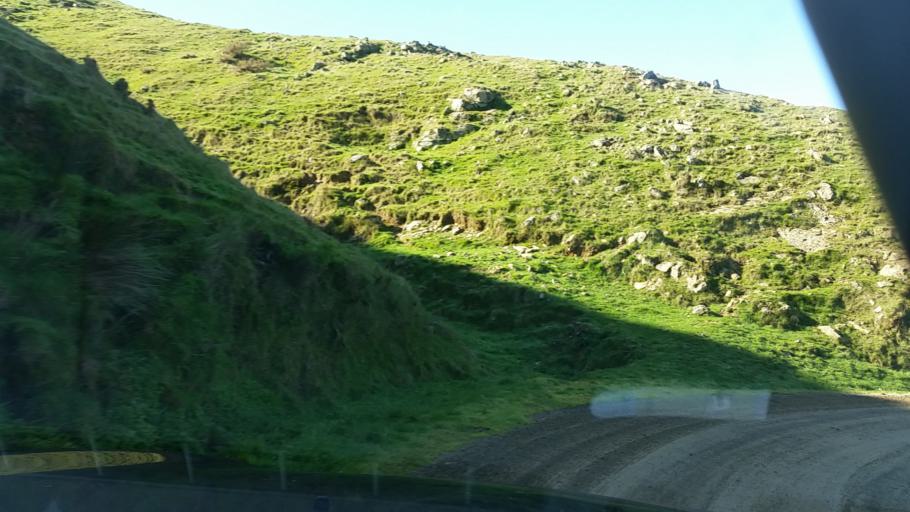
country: NZ
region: Marlborough
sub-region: Marlborough District
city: Picton
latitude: -40.9862
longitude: 173.8114
